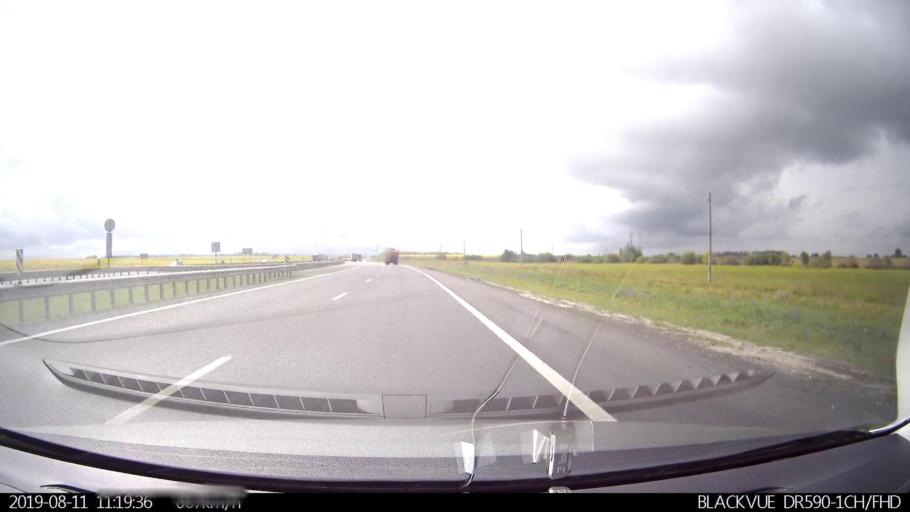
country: RU
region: Ulyanovsk
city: Novoul'yanovsk
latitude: 54.1669
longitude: 48.2647
